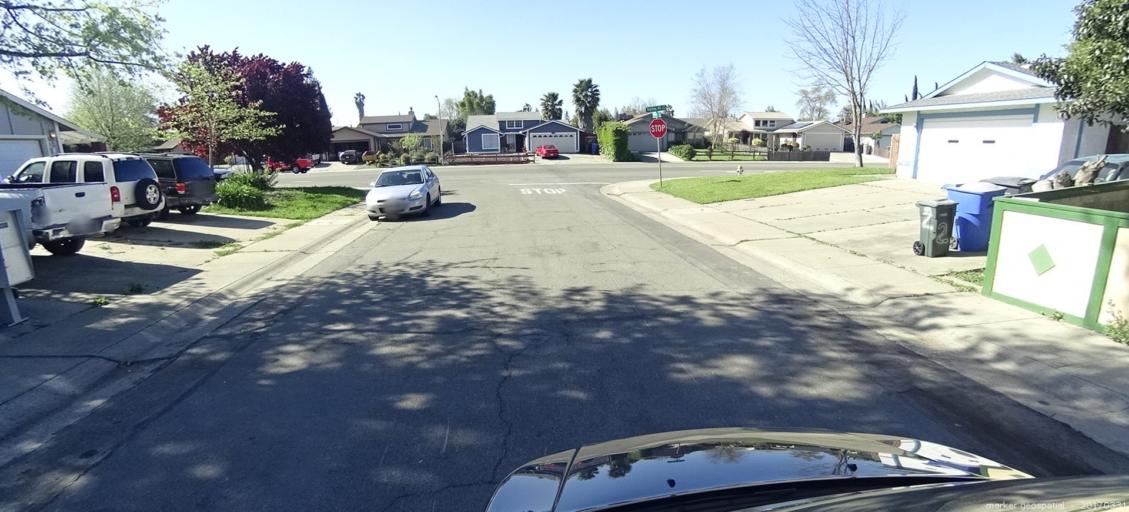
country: US
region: California
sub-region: Sacramento County
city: Parkway
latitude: 38.4671
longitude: -121.4436
